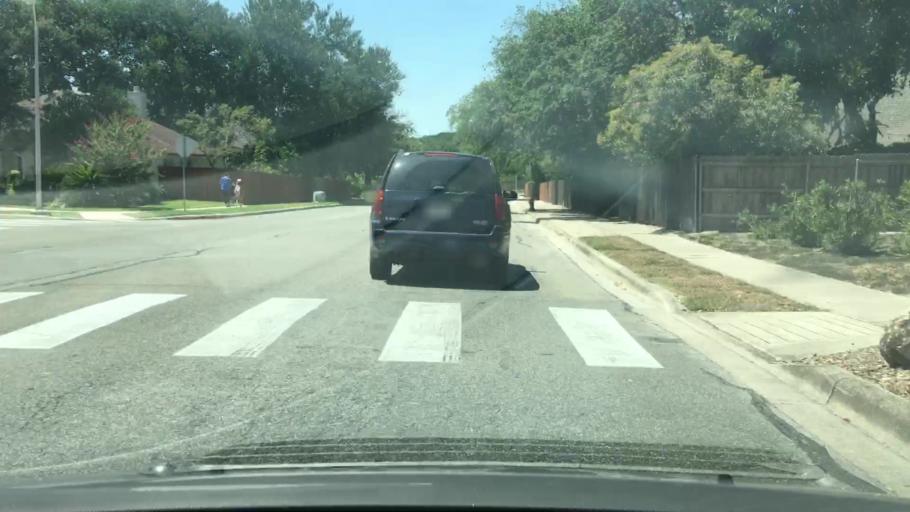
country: US
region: Texas
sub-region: Guadalupe County
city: Schertz
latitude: 29.5803
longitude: -98.2552
